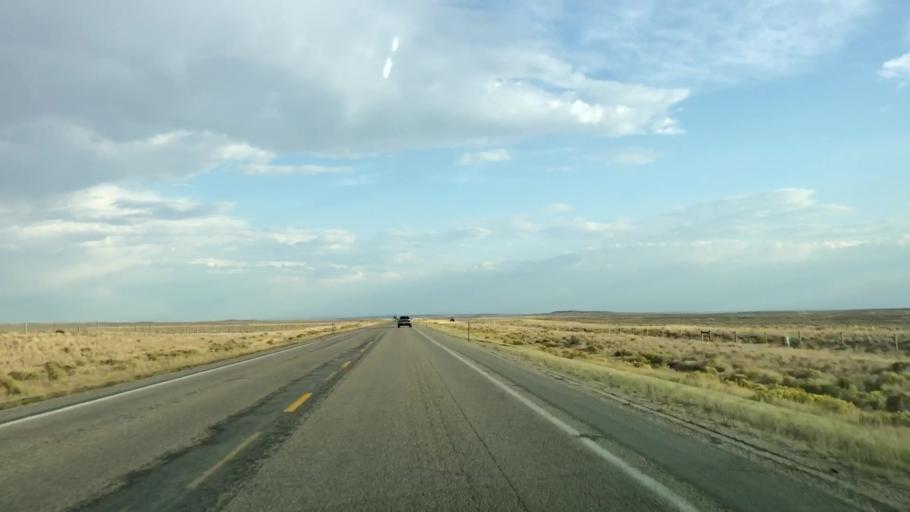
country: US
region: Wyoming
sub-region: Sublette County
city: Pinedale
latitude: 42.4047
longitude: -109.5488
